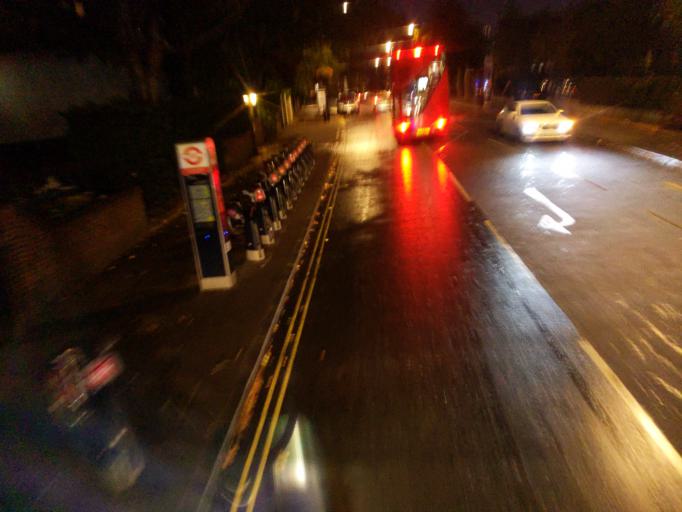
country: GB
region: England
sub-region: Greater London
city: Belsize Park
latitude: 51.5308
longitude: -0.1766
